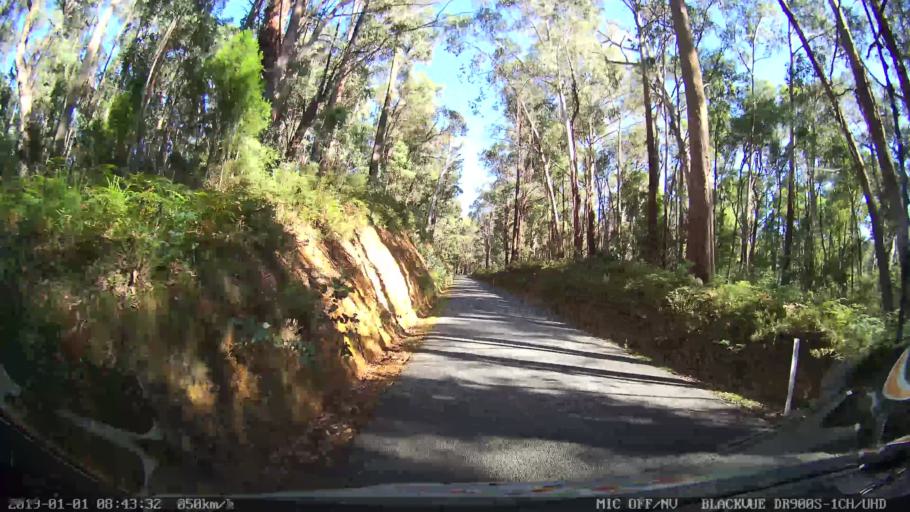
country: AU
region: New South Wales
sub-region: Snowy River
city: Jindabyne
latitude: -36.3166
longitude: 148.1927
